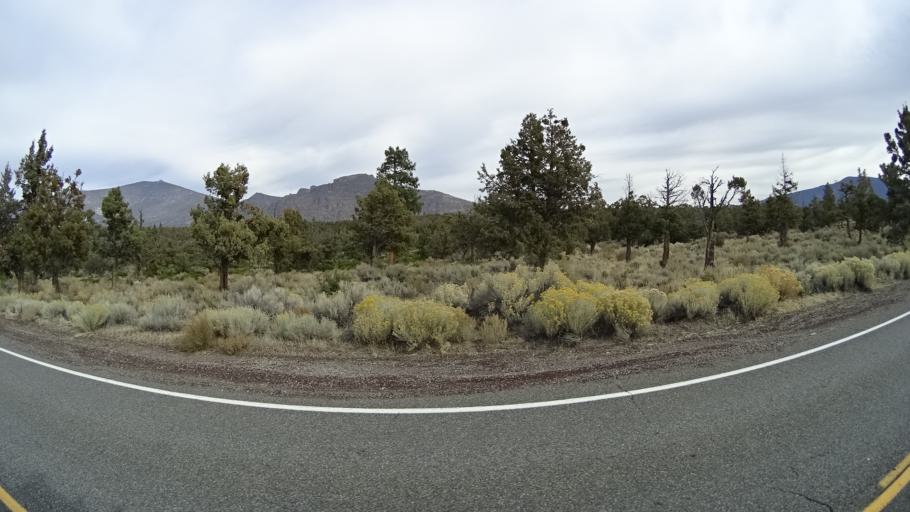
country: US
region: California
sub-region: Siskiyou County
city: Weed
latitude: 41.5538
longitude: -122.2525
